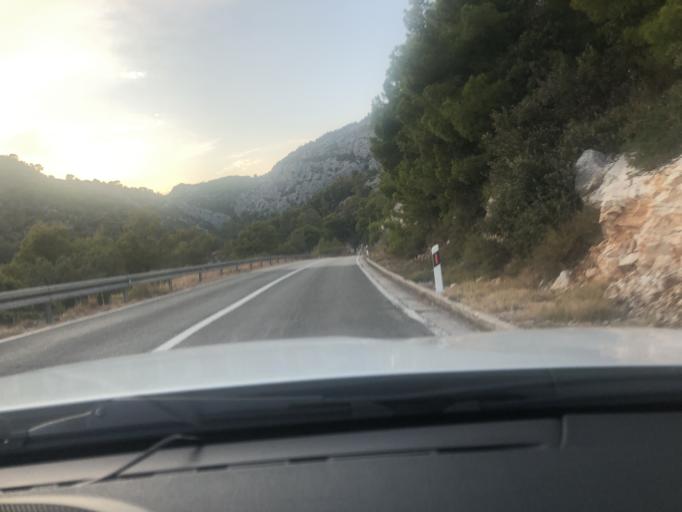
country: HR
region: Splitsko-Dalmatinska
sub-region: Grad Hvar
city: Hvar
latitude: 43.1640
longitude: 16.4851
